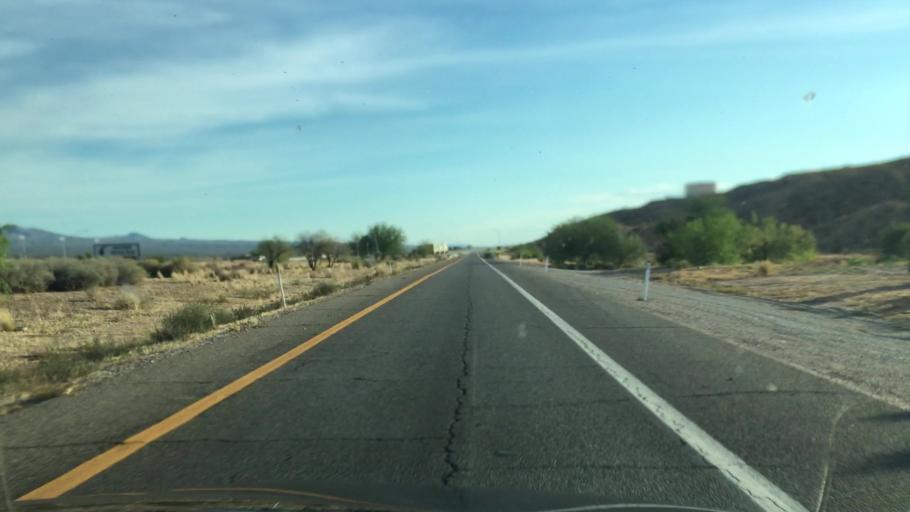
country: US
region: Nevada
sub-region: Clark County
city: Mesquite
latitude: 36.8128
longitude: -114.0659
